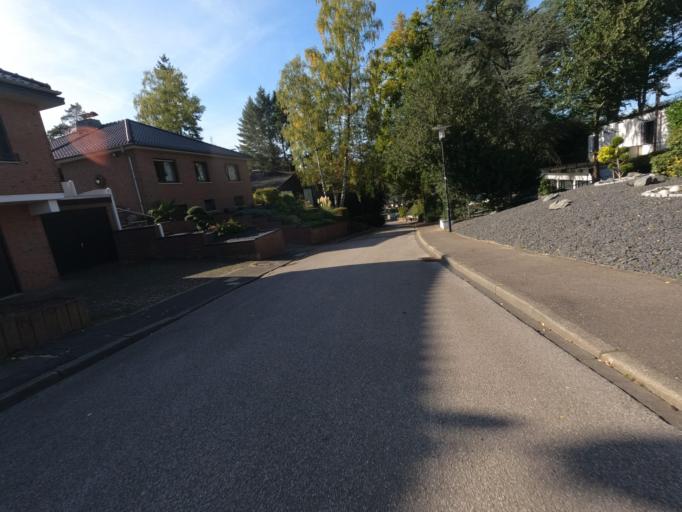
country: DE
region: North Rhine-Westphalia
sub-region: Regierungsbezirk Koln
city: Wassenberg
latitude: 51.1024
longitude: 6.1731
